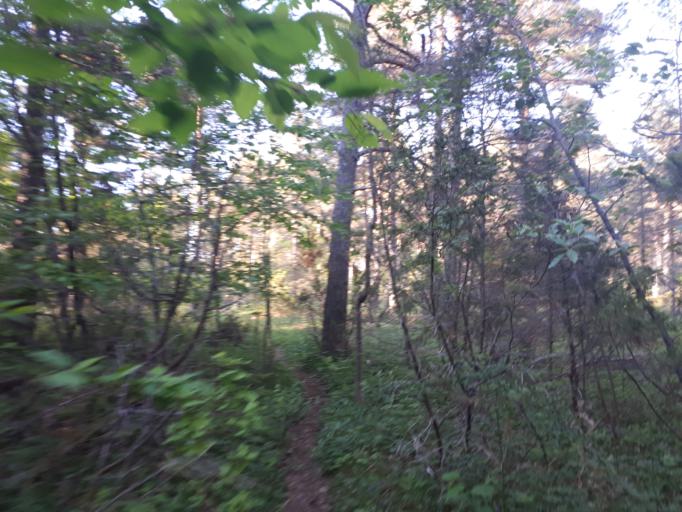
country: SE
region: Gotland
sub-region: Gotland
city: Visby
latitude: 57.6044
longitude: 18.2893
